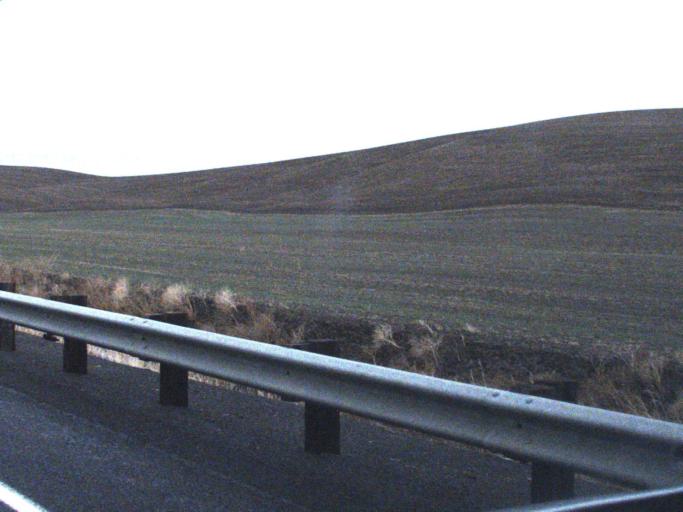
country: US
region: Washington
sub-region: Walla Walla County
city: Waitsburg
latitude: 46.2080
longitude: -118.1376
